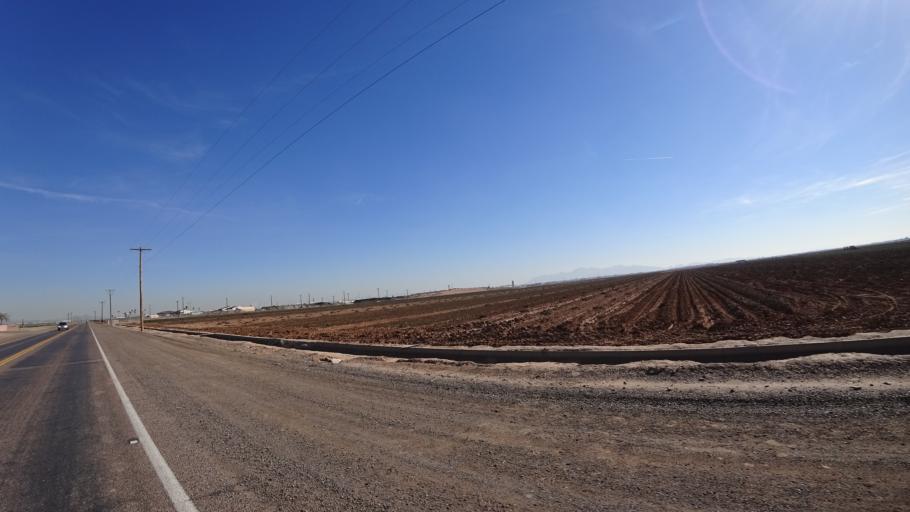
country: US
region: Arizona
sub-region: Maricopa County
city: Citrus Park
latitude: 33.5515
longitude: -112.3871
